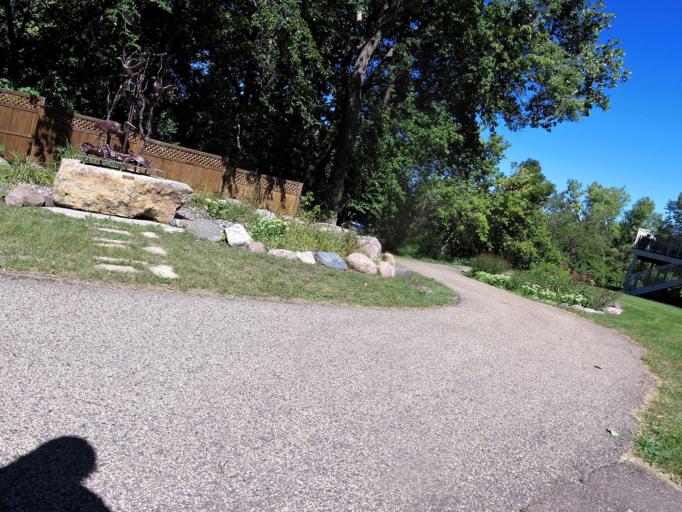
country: US
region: Minnesota
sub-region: Scott County
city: Prior Lake
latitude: 44.7156
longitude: -93.4252
